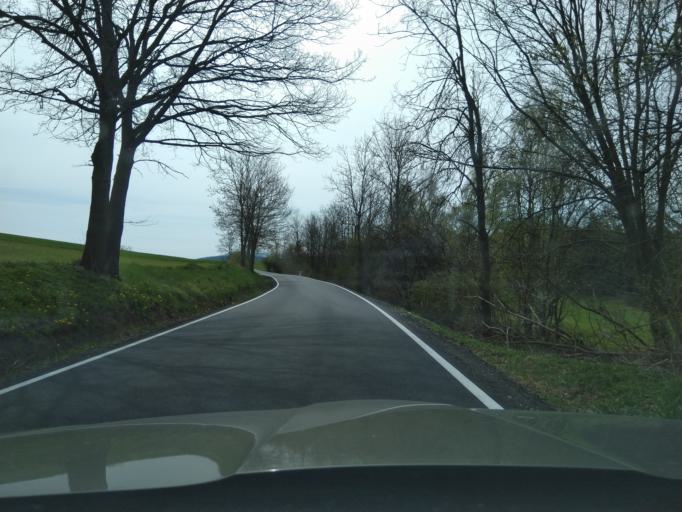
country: CZ
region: Jihocesky
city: Vacov
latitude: 49.1258
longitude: 13.7407
